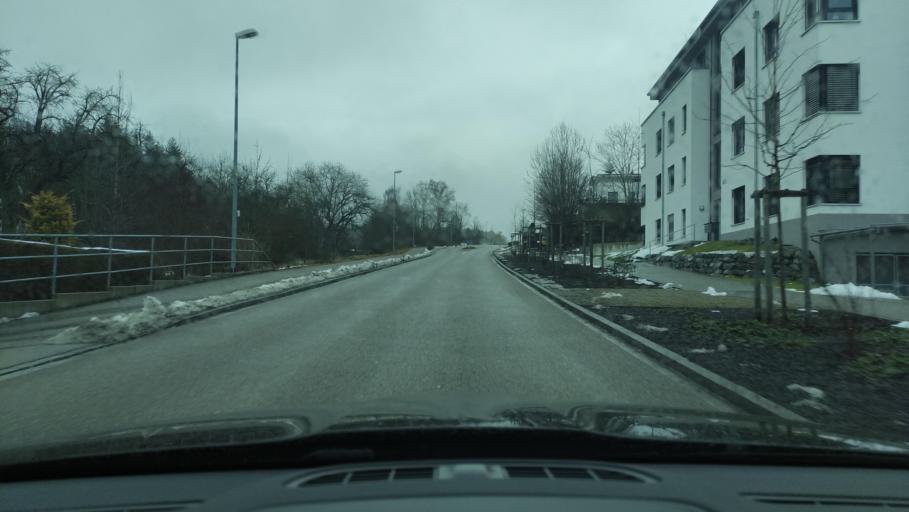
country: DE
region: Bavaria
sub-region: Swabia
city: Weissenhorn
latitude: 48.2971
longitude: 10.1700
